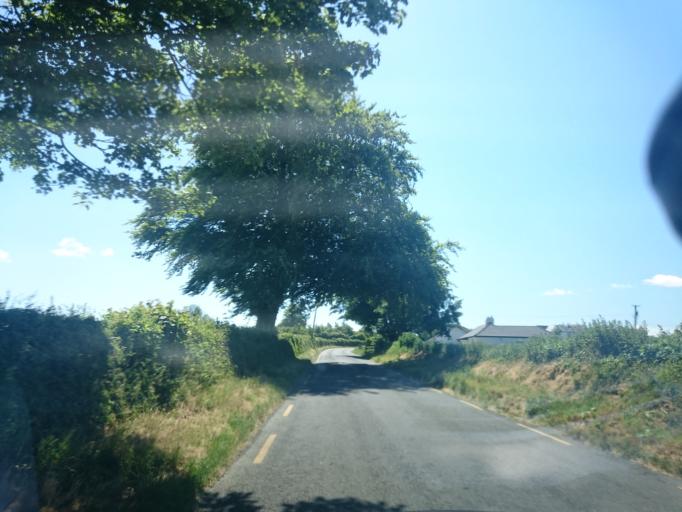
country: IE
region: Leinster
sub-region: County Carlow
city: Bagenalstown
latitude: 52.6235
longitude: -6.9912
